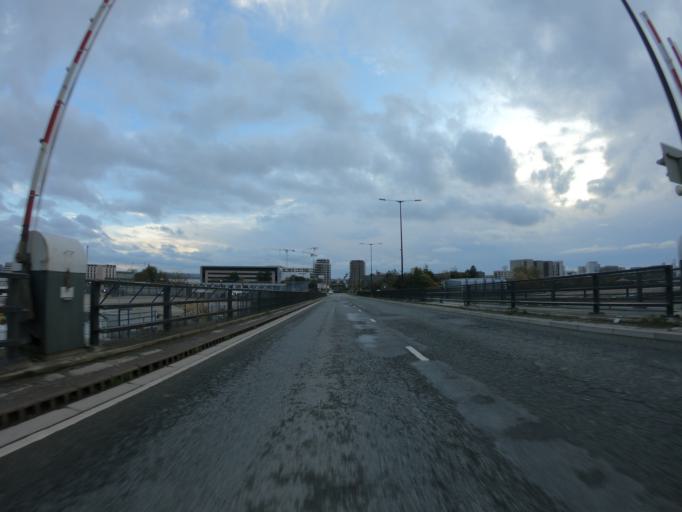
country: GB
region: England
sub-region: Greater London
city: Woolwich
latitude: 51.5060
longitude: 0.0399
